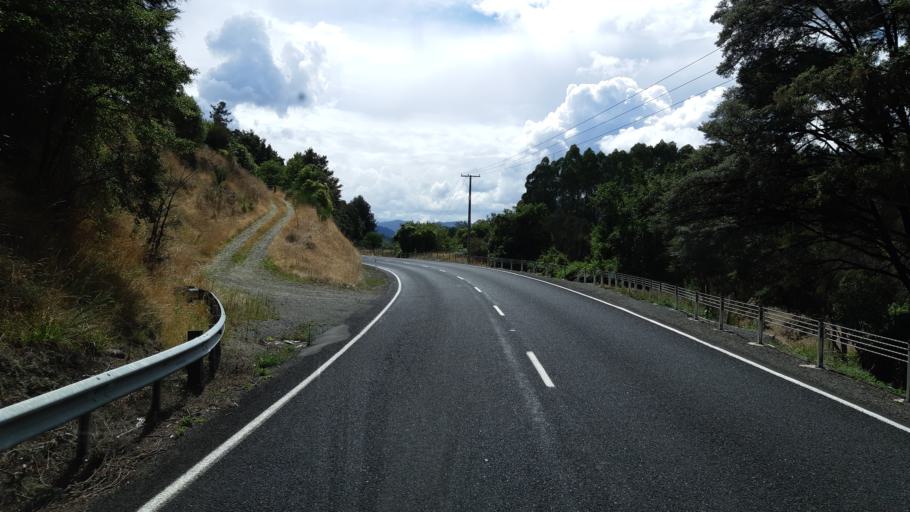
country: NZ
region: Tasman
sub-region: Tasman District
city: Wakefield
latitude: -41.4952
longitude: 172.7963
